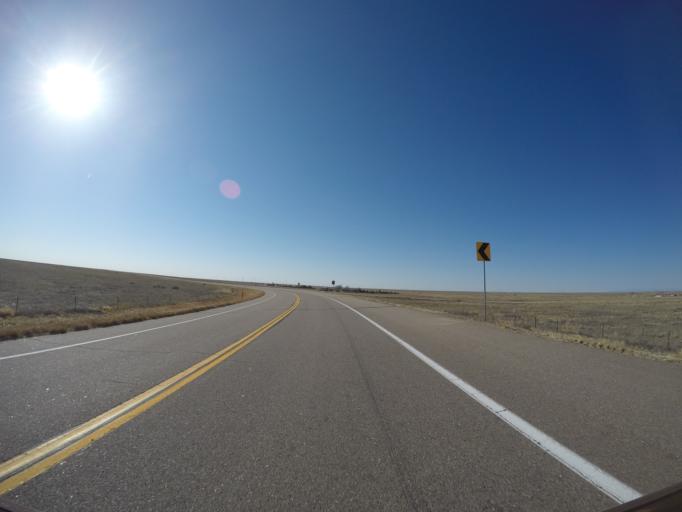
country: US
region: Colorado
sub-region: Otero County
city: La Junta
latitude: 37.9378
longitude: -103.5450
